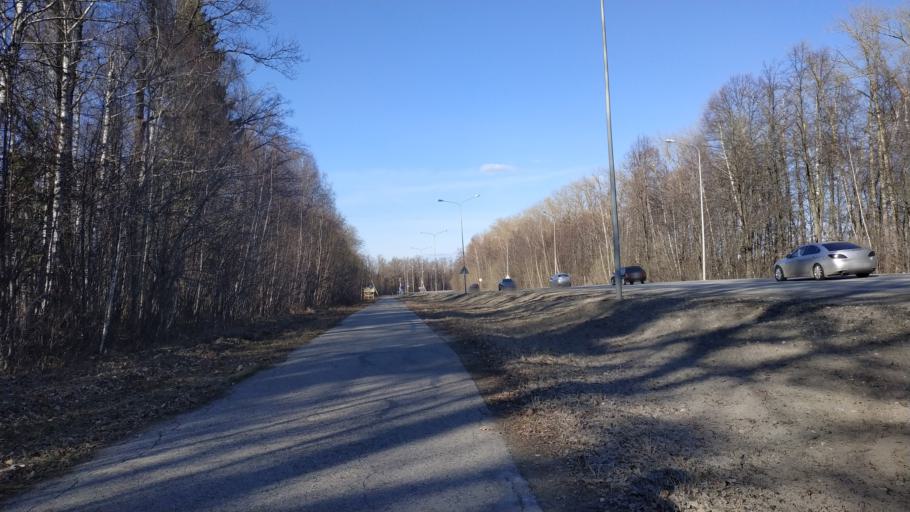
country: RU
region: Chuvashia
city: Ishley
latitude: 56.1287
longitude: 47.0701
